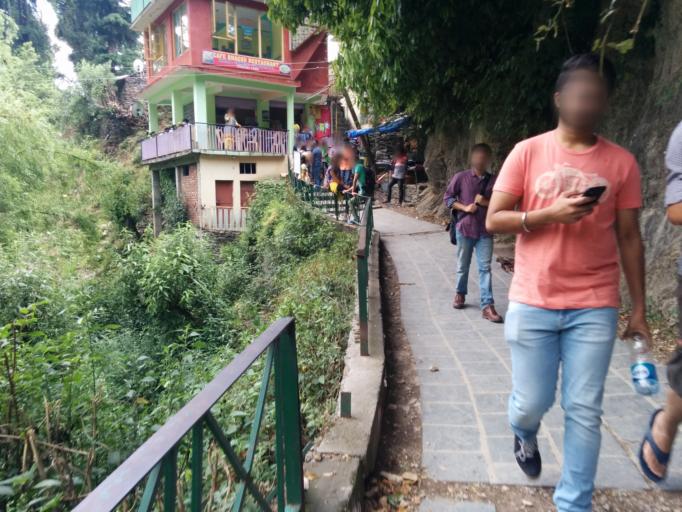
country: IN
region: Himachal Pradesh
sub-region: Kangra
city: Dharmsala
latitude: 32.2445
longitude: 76.3350
